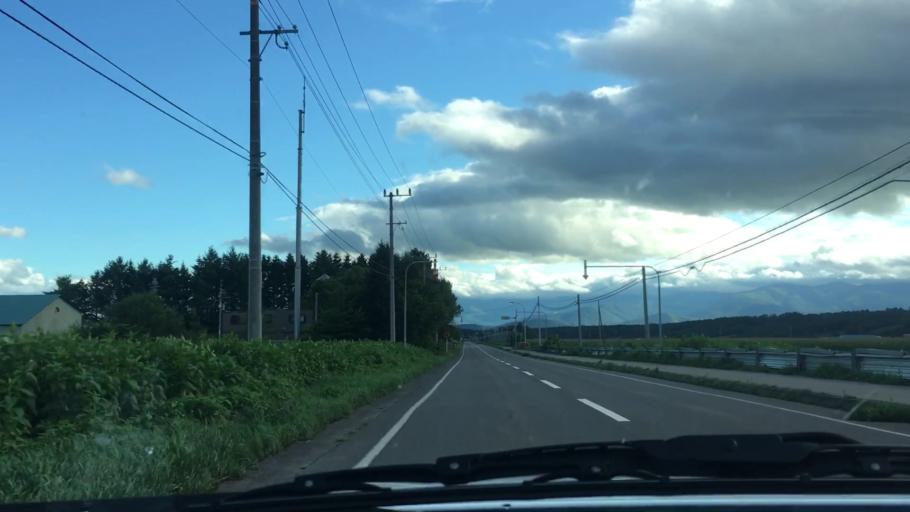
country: JP
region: Hokkaido
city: Otofuke
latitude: 43.1453
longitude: 142.8978
